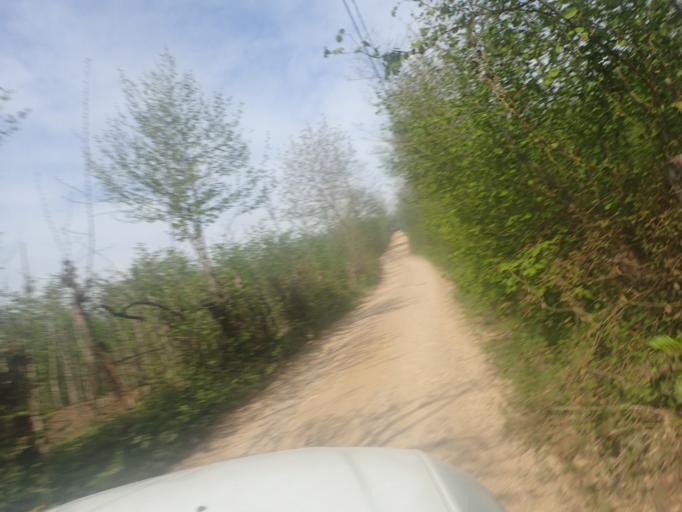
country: TR
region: Ordu
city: Catalpinar
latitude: 40.8820
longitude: 37.4907
